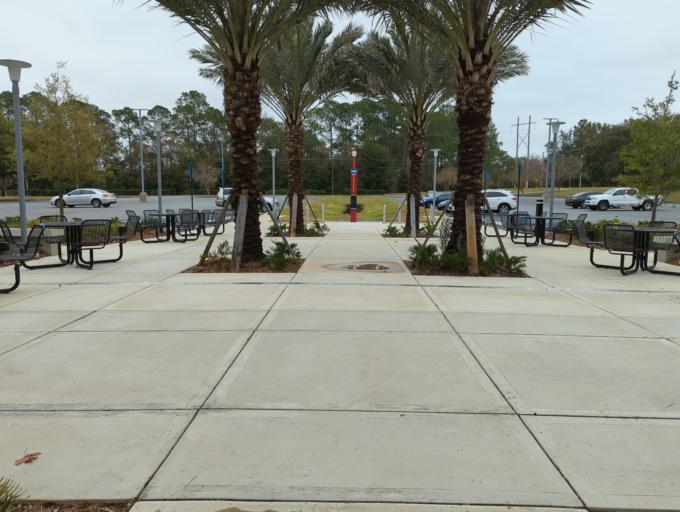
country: US
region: Florida
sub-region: Leon County
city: Tallahassee
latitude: 30.4200
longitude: -84.3173
